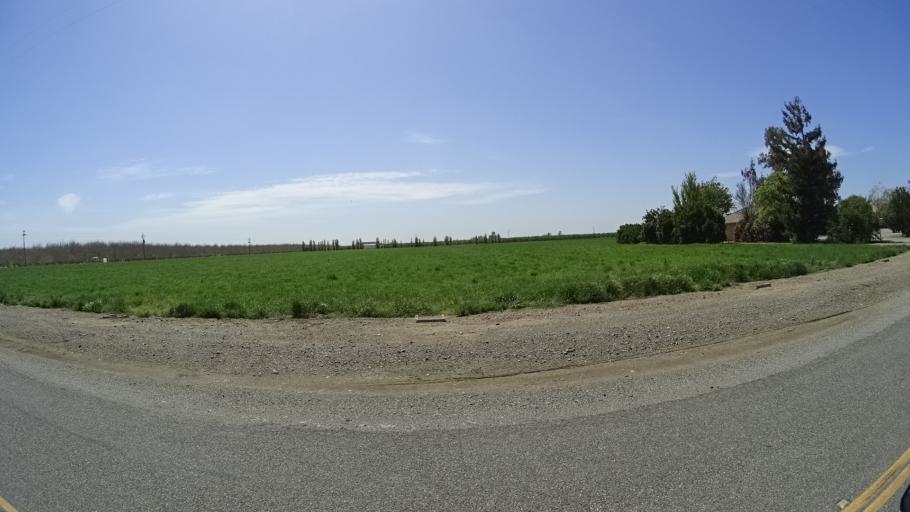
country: US
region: California
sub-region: Glenn County
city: Hamilton City
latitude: 39.6522
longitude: -122.1042
